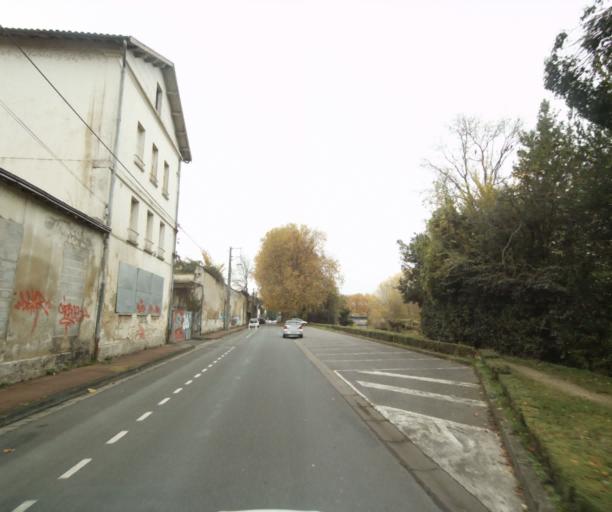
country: FR
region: Poitou-Charentes
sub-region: Departement de la Charente-Maritime
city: Saintes
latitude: 45.7395
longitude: -0.6381
